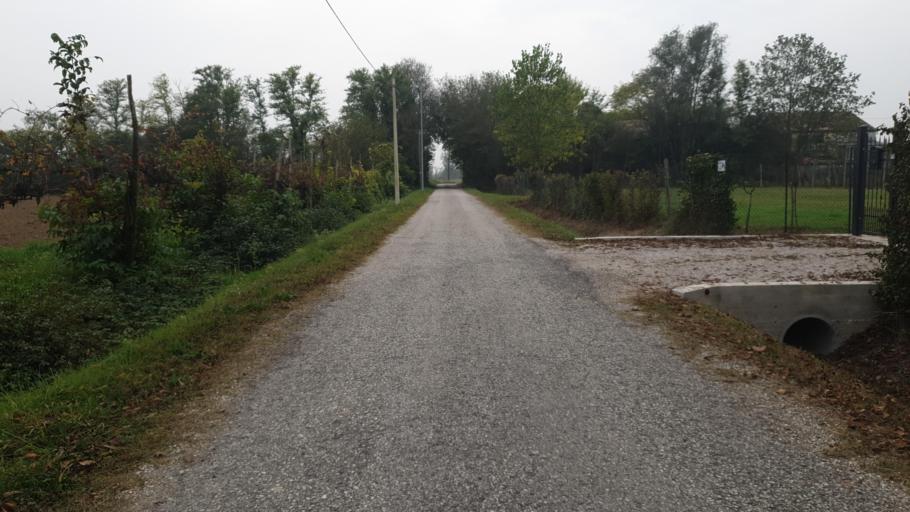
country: IT
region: Veneto
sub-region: Provincia di Padova
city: Casalserugo
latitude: 45.2941
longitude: 11.9208
